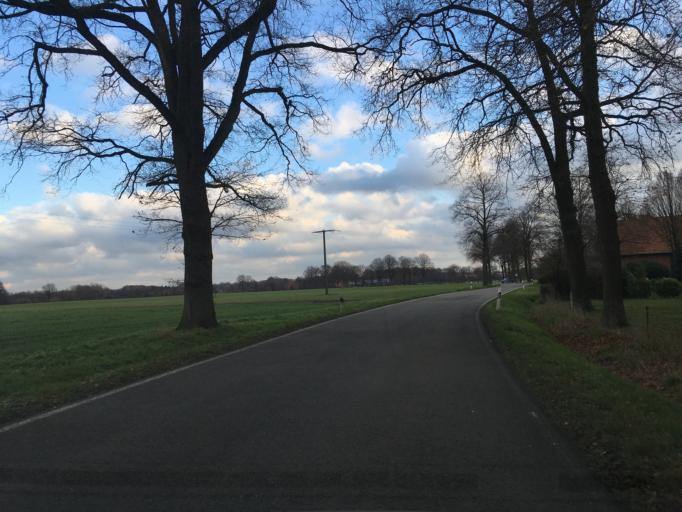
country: DE
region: North Rhine-Westphalia
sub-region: Regierungsbezirk Munster
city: Gescher
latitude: 51.9523
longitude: 7.0756
